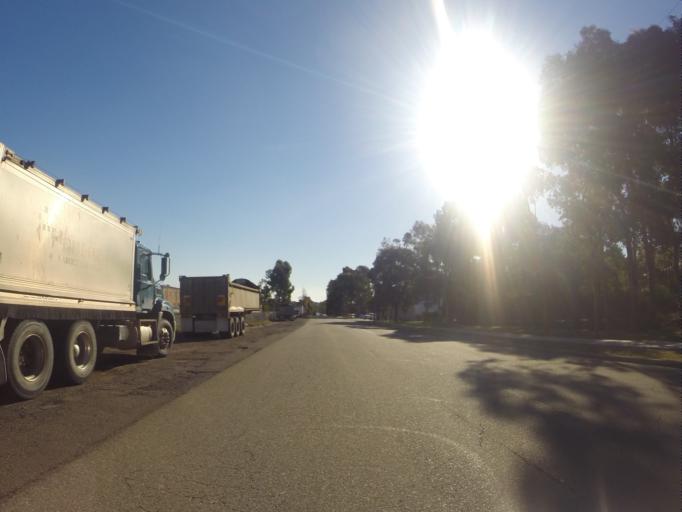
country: AU
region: New South Wales
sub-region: Bankstown
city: Regents Park
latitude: -33.8822
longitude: 151.0206
